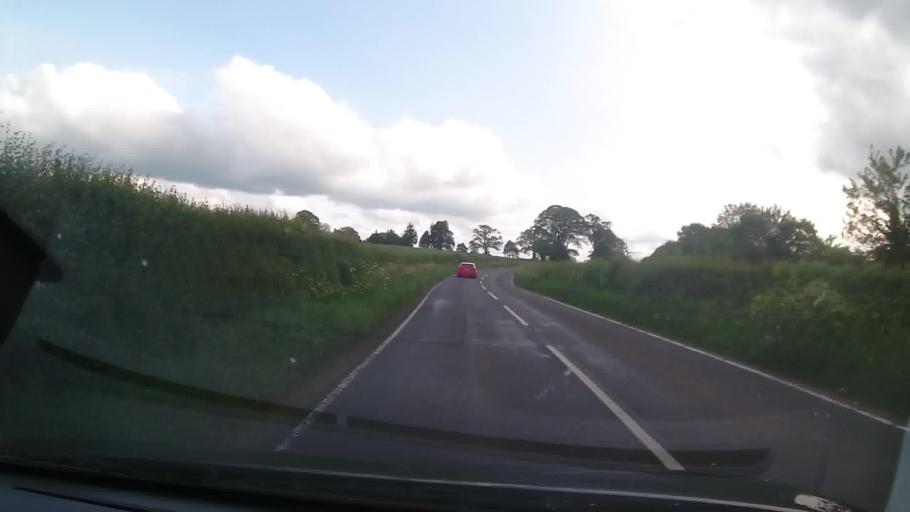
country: GB
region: England
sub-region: Shropshire
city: Clive
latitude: 52.8246
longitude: -2.7383
